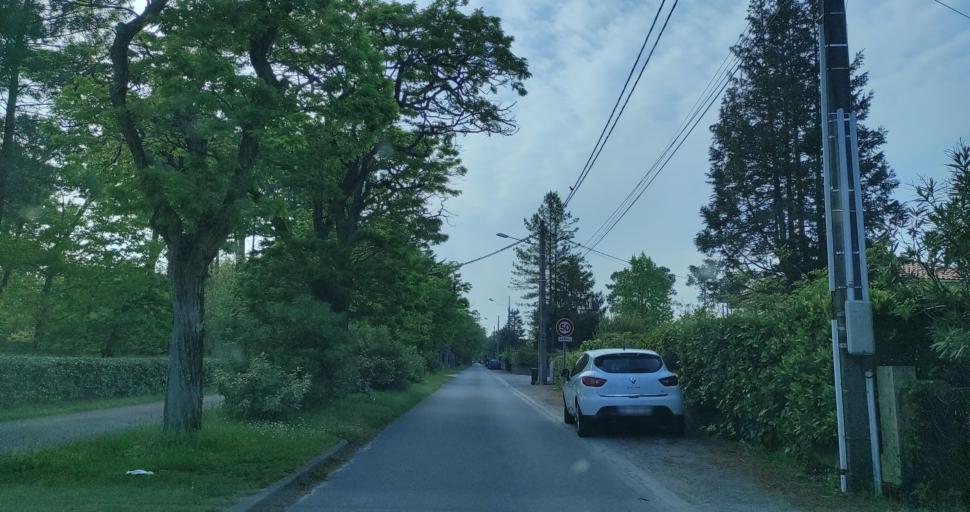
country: FR
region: Aquitaine
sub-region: Departement de la Gironde
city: Ares
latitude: 44.7544
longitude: -1.1291
